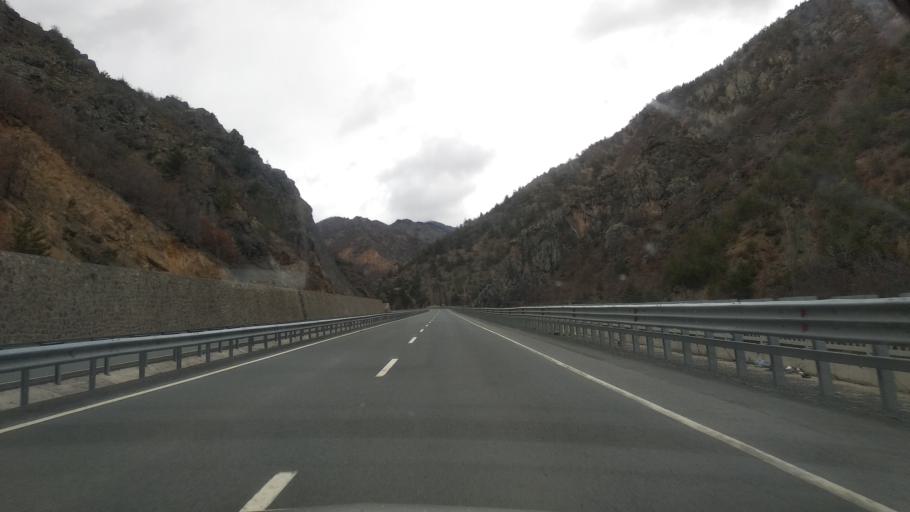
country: TR
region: Gumushane
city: Torul
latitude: 40.6278
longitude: 39.3381
